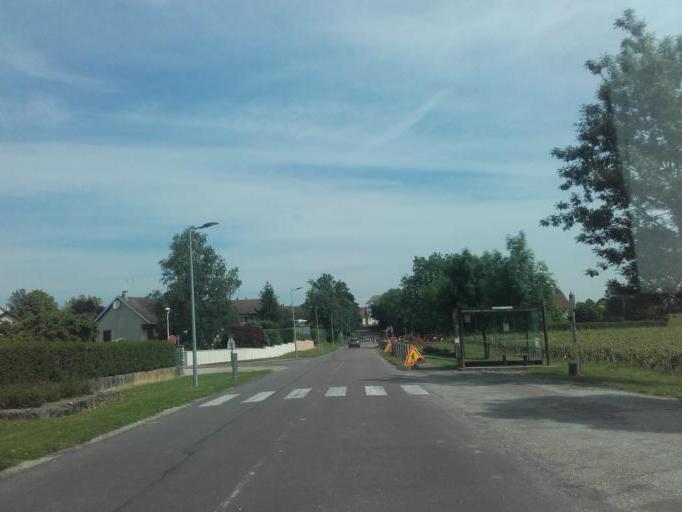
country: FR
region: Bourgogne
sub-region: Departement de la Cote-d'Or
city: Corpeau
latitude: 46.9251
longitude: 4.7527
